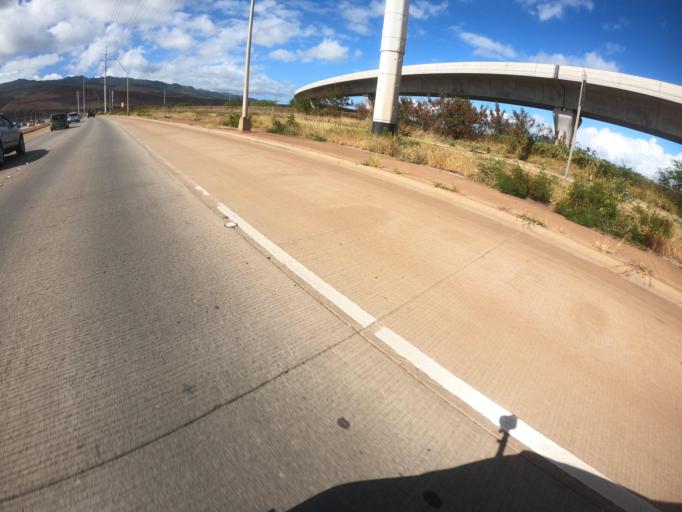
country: US
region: Hawaii
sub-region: Honolulu County
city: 'Ewa Villages
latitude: 21.3588
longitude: -158.0514
